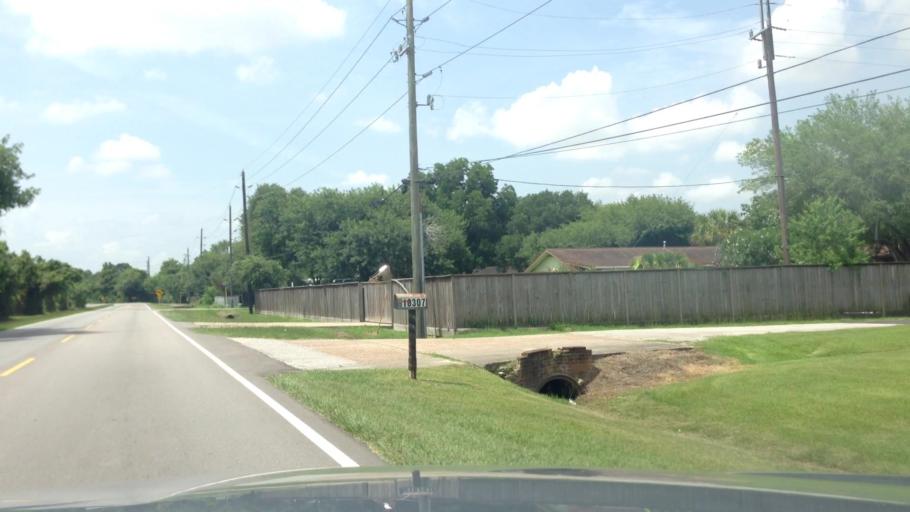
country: US
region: Texas
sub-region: Harris County
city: Jersey Village
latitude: 29.9183
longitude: -95.5480
